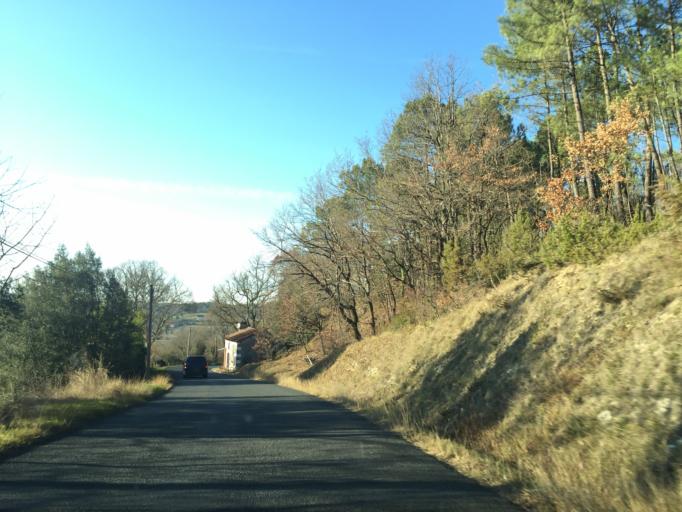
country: FR
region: Aquitaine
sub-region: Departement de la Dordogne
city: Neuvic
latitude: 45.1381
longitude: 0.4621
